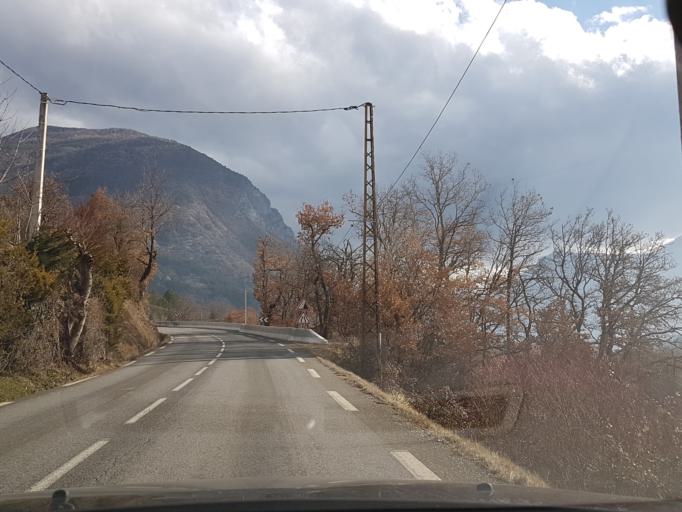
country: FR
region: Provence-Alpes-Cote d'Azur
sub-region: Departement des Hautes-Alpes
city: Tallard
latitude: 44.4764
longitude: 6.1118
